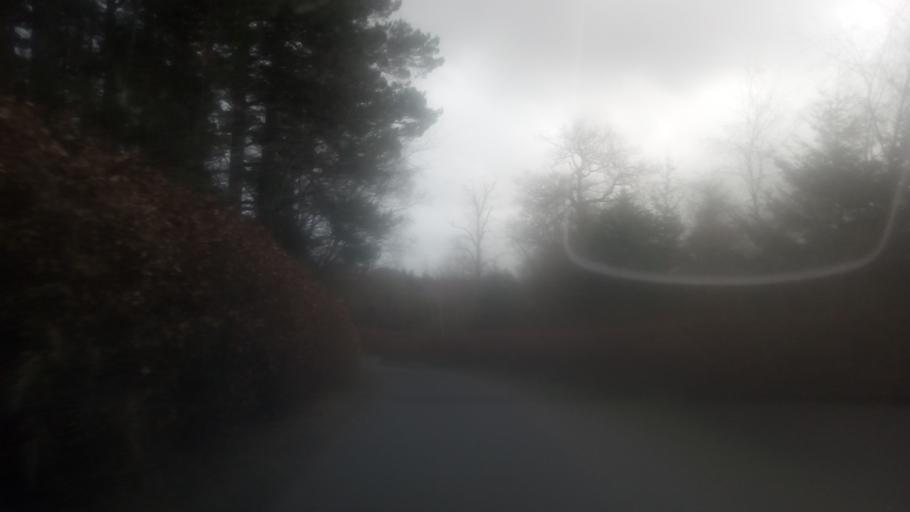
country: GB
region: Scotland
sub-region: The Scottish Borders
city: Jedburgh
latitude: 55.4797
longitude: -2.5257
